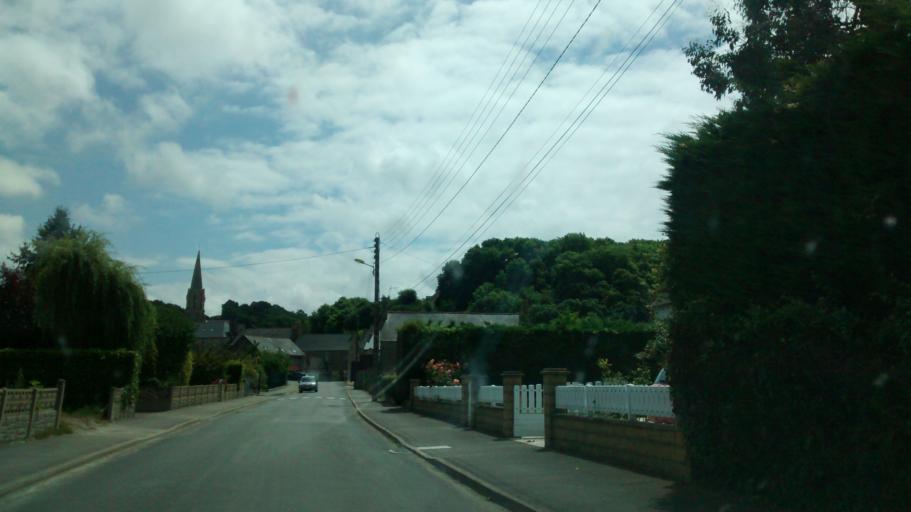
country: FR
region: Brittany
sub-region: Departement d'Ille-et-Vilaine
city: Saint-Broladre
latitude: 48.5882
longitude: -1.6593
